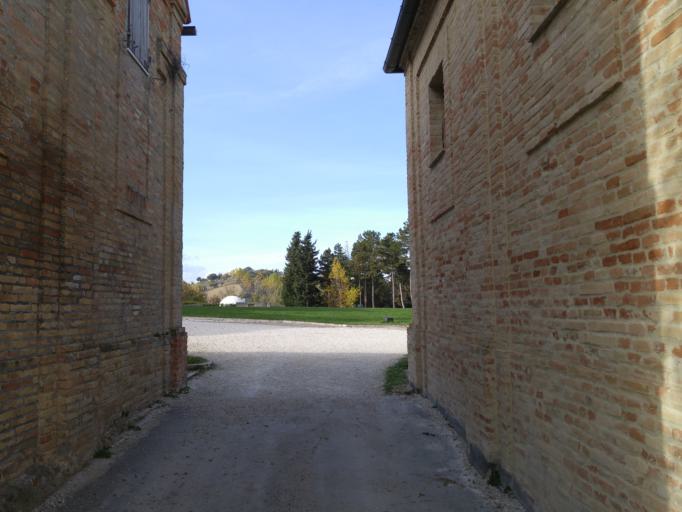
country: IT
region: The Marches
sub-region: Provincia di Pesaro e Urbino
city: Saltara
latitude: 43.7560
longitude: 12.8909
